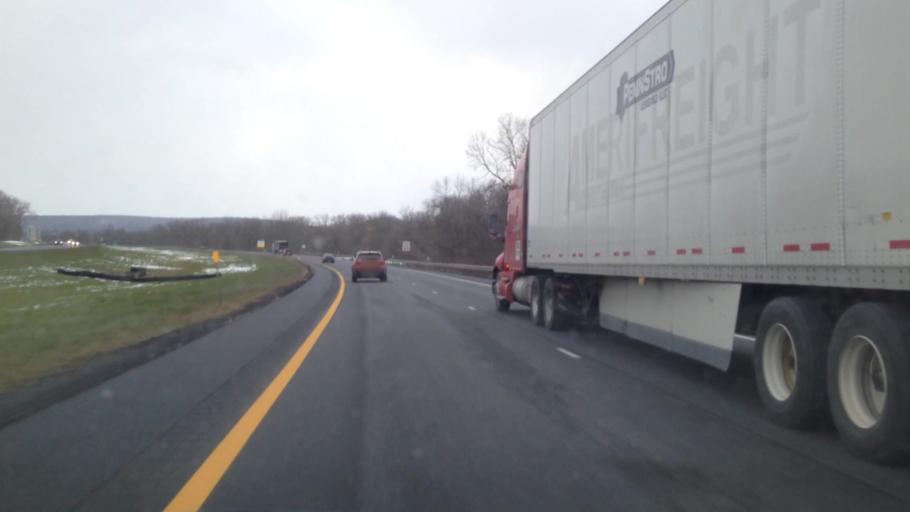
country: US
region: New York
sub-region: Montgomery County
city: Fonda
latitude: 42.9482
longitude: -74.3822
